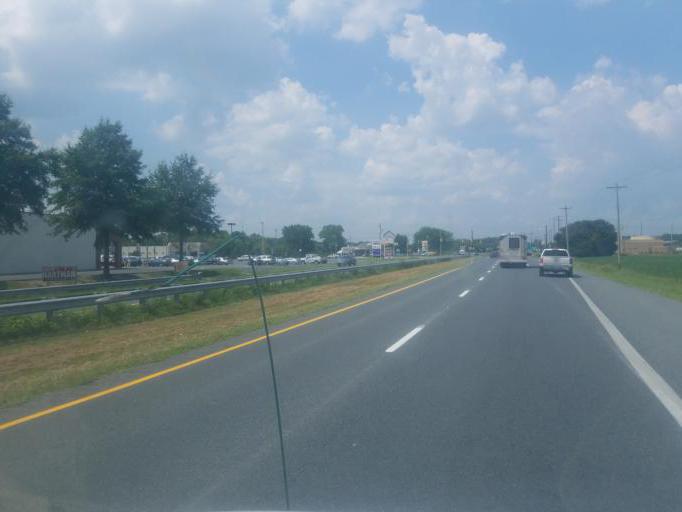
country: US
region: Maryland
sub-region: Worcester County
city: Berlin
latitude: 38.3335
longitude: -75.2102
